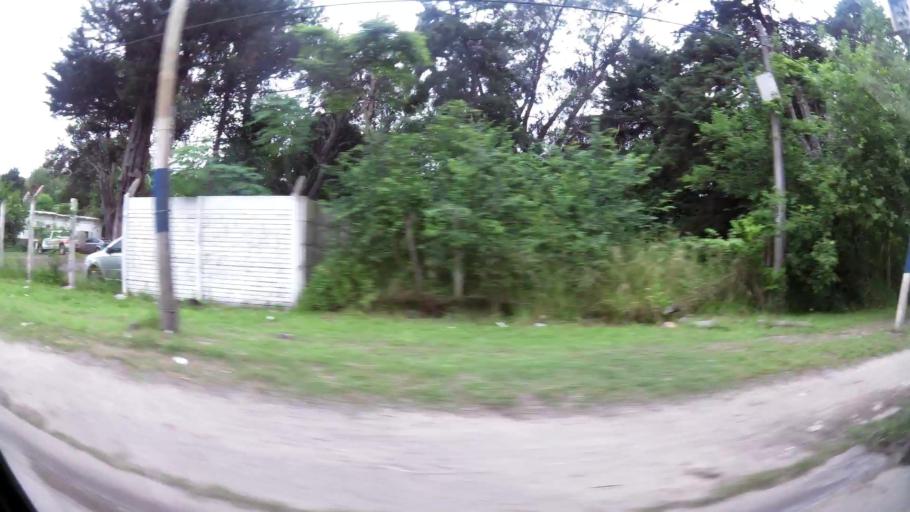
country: AR
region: Buenos Aires
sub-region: Partido de La Plata
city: La Plata
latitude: -34.9580
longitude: -58.0071
